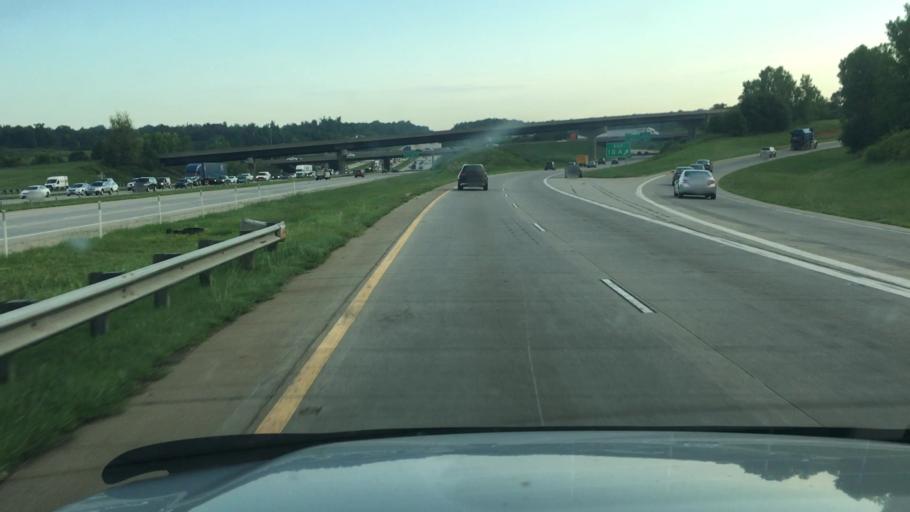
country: US
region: North Carolina
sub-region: Gaston County
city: Belmont
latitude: 35.2450
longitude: -80.9689
